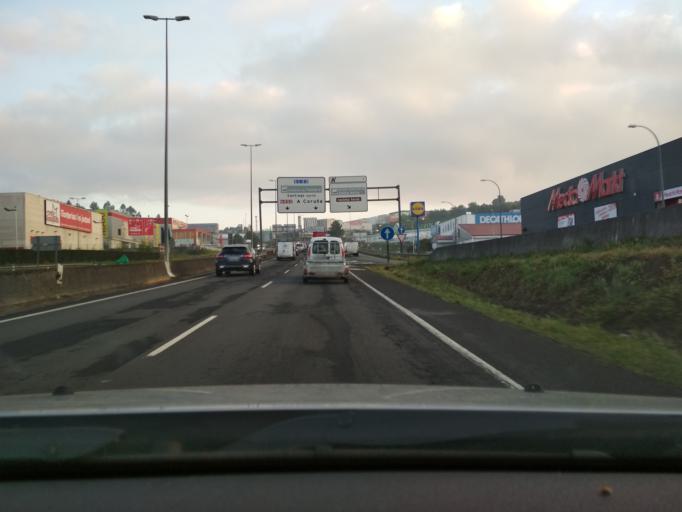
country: ES
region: Galicia
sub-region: Provincia da Coruna
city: Santiago de Compostela
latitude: 42.8996
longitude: -8.5102
